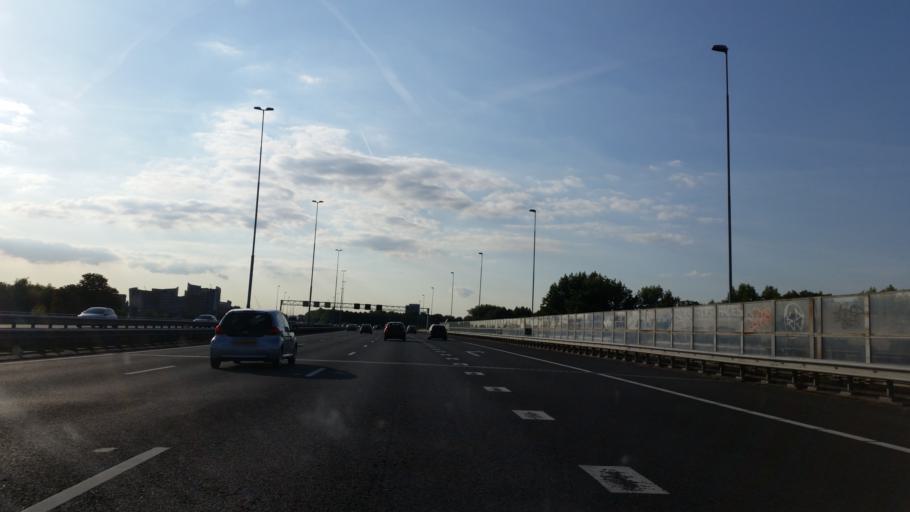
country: NL
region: North Holland
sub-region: Gemeente Ouder-Amstel
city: Ouderkerk aan de Amstel
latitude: 52.2945
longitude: 4.8922
